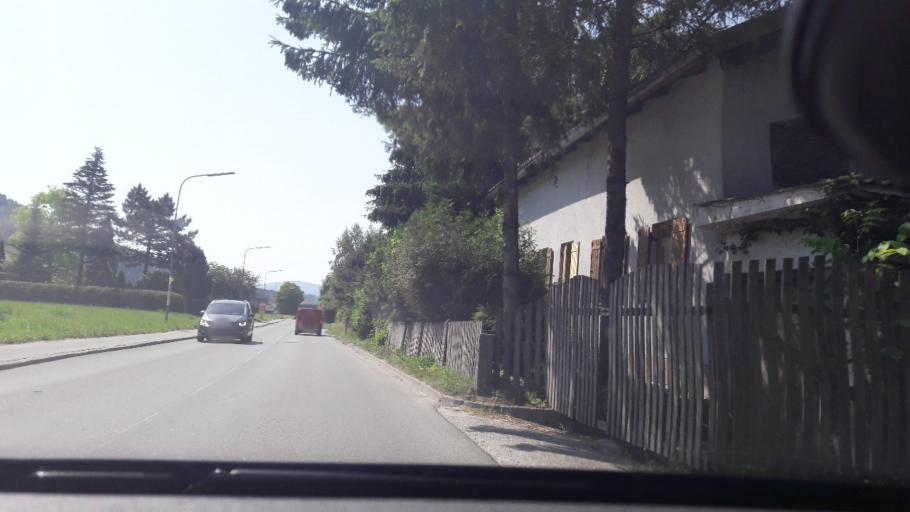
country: AT
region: Styria
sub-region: Politischer Bezirk Voitsberg
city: Kohlschwarz
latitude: 47.0923
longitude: 15.1205
